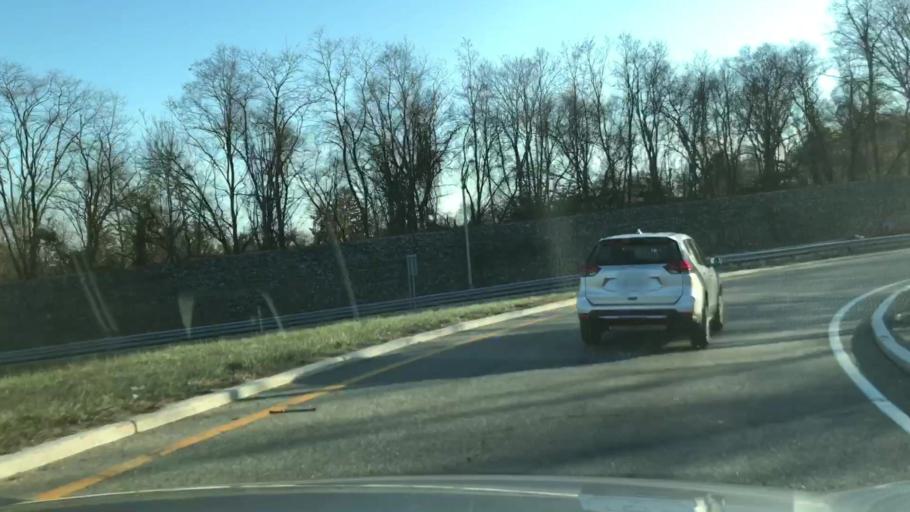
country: US
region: New Jersey
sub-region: Morris County
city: Riverdale
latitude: 40.9870
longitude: -74.3075
